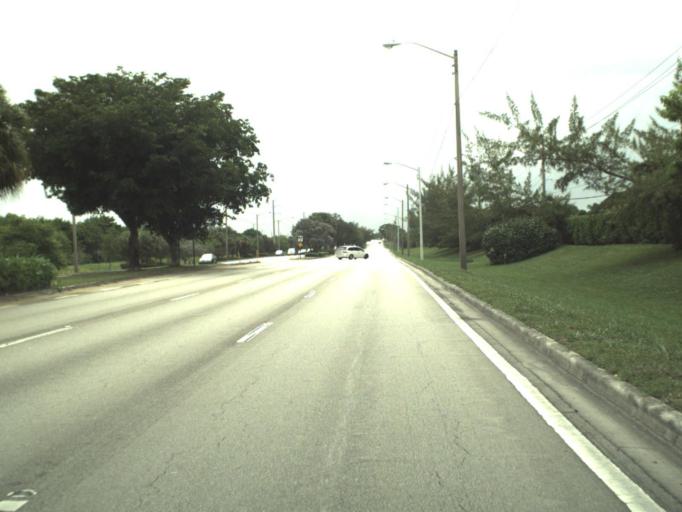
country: US
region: Florida
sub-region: Palm Beach County
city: Boca Del Mar
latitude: 26.3504
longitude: -80.1623
